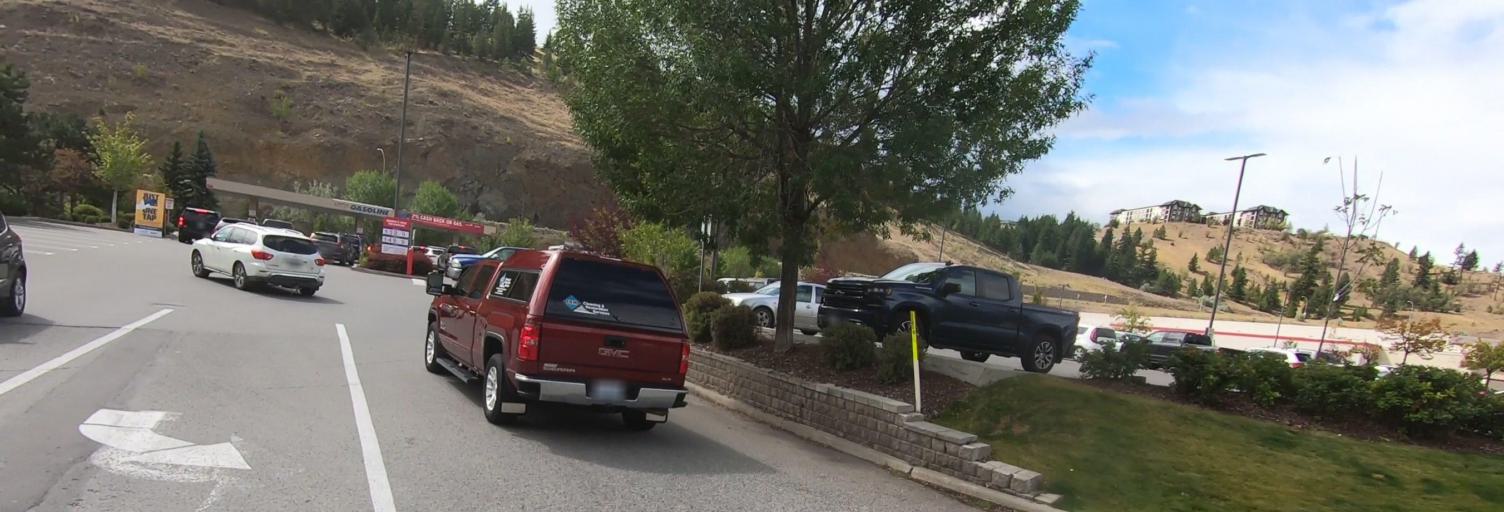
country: CA
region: British Columbia
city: Kamloops
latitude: 50.6545
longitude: -120.3866
